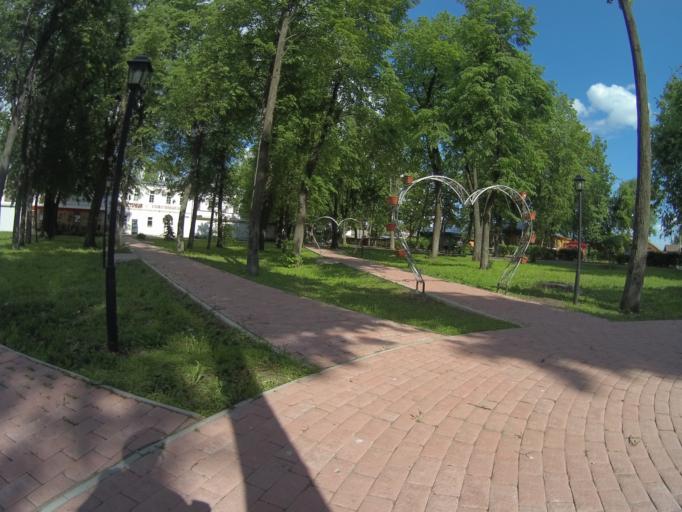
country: RU
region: Vladimir
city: Suzdal'
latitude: 56.4174
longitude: 40.4435
